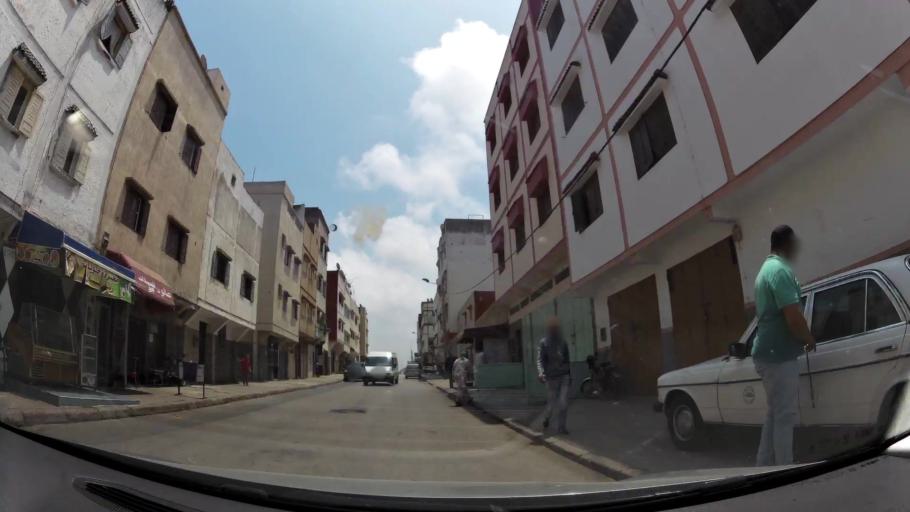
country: MA
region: Rabat-Sale-Zemmour-Zaer
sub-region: Rabat
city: Rabat
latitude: 33.9814
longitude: -6.8792
